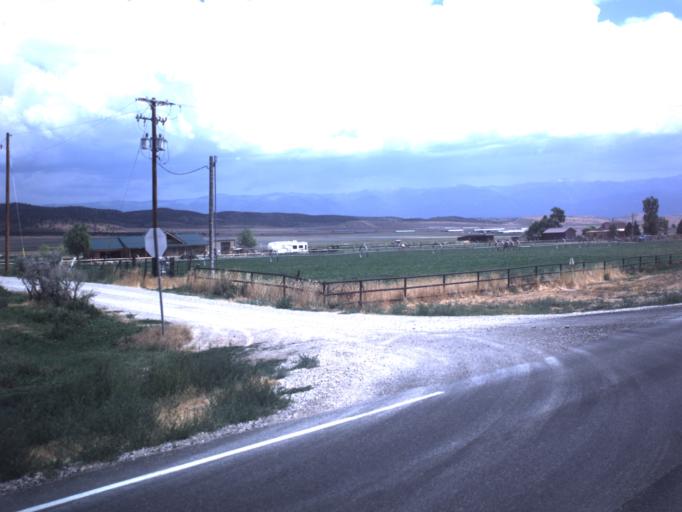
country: US
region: Utah
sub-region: Sanpete County
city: Fountain Green
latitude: 39.6072
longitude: -111.6251
